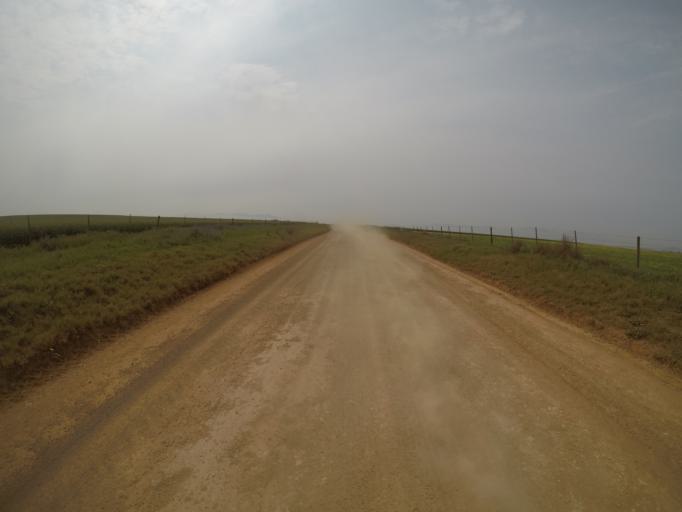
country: ZA
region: Western Cape
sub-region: City of Cape Town
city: Kraaifontein
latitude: -33.7216
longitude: 18.6748
